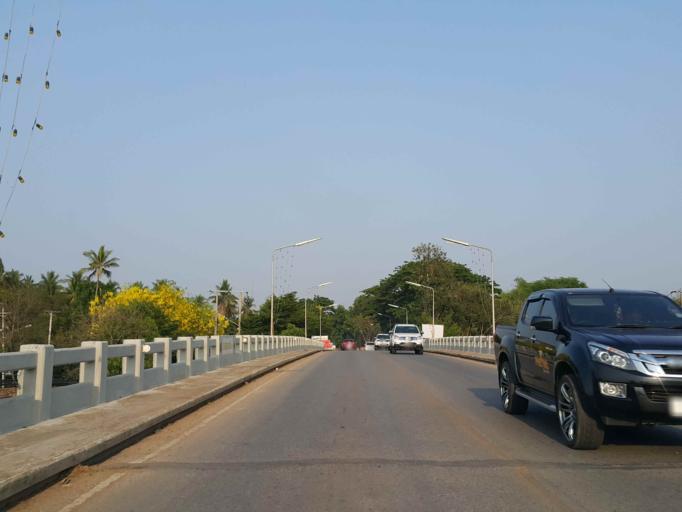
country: TH
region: Sukhothai
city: Sawankhalok
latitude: 17.3025
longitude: 99.8300
